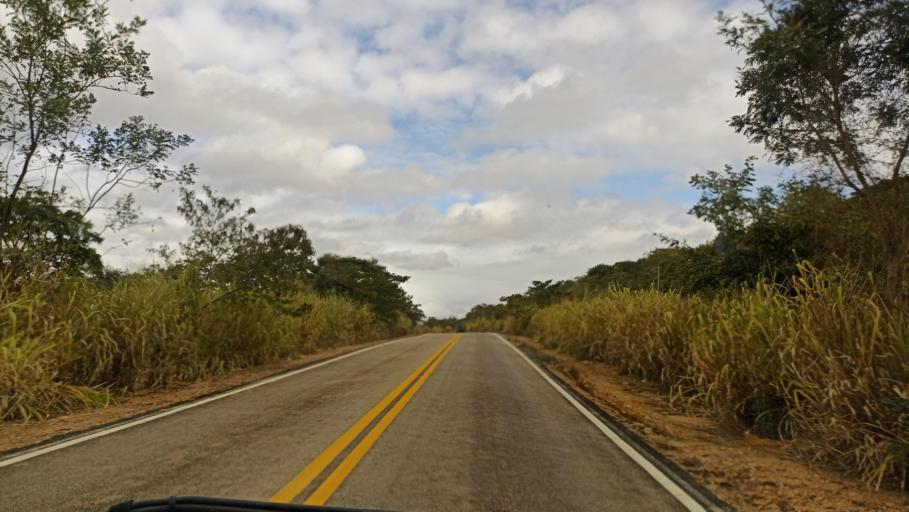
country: BR
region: Minas Gerais
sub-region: Joaima
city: Joaima
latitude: -16.6923
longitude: -40.9585
